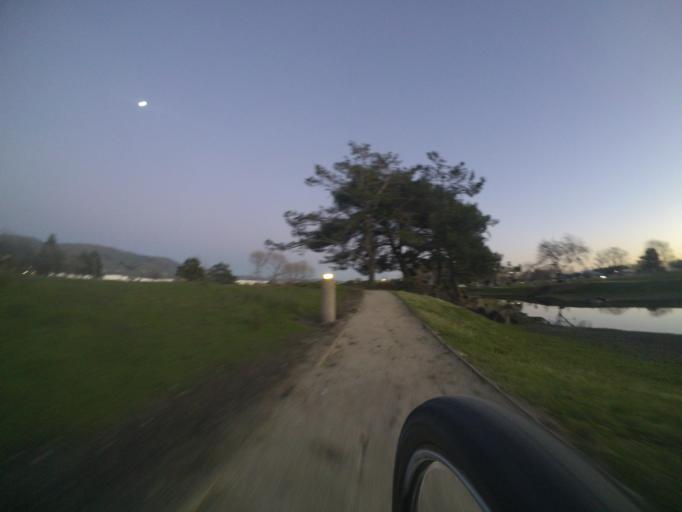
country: US
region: California
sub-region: Santa Clara County
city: Milpitas
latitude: 37.4781
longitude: -121.9379
